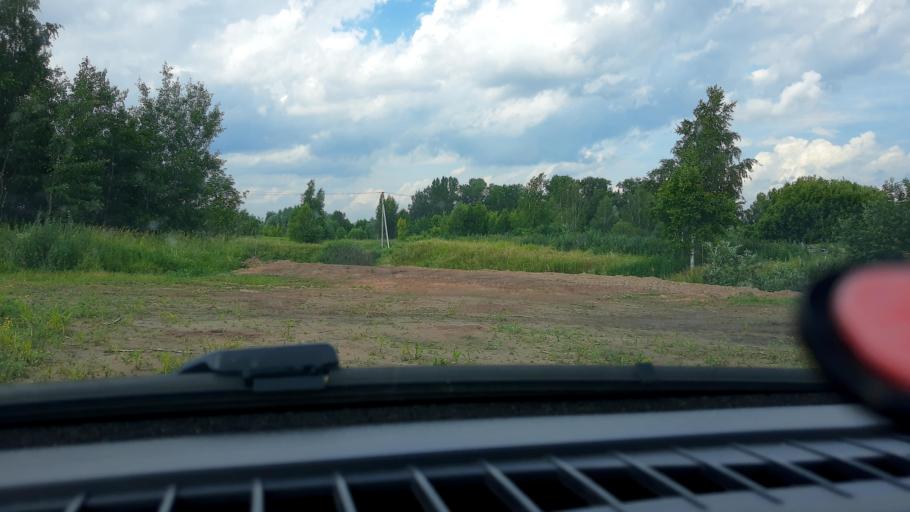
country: RU
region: Nizjnij Novgorod
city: Afonino
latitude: 56.2146
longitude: 44.1133
